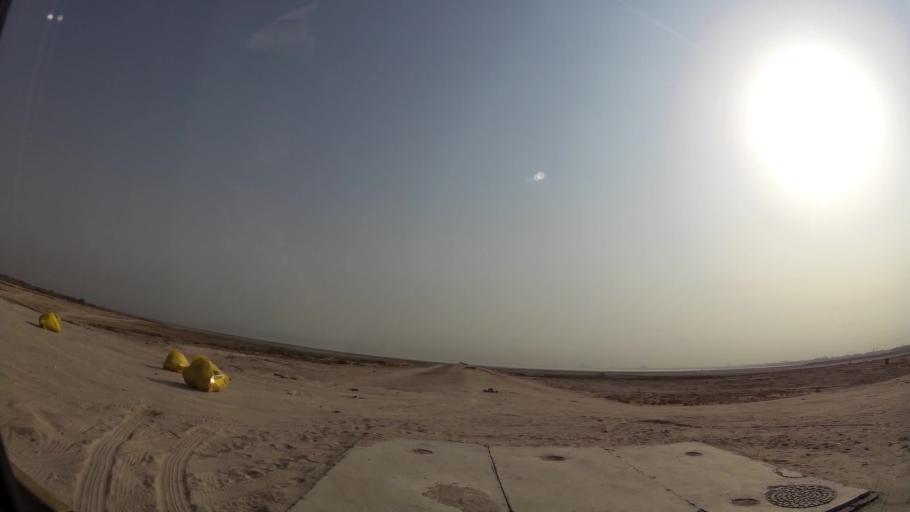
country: KW
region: Al Asimah
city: Ar Rabiyah
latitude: 29.3314
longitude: 47.8159
